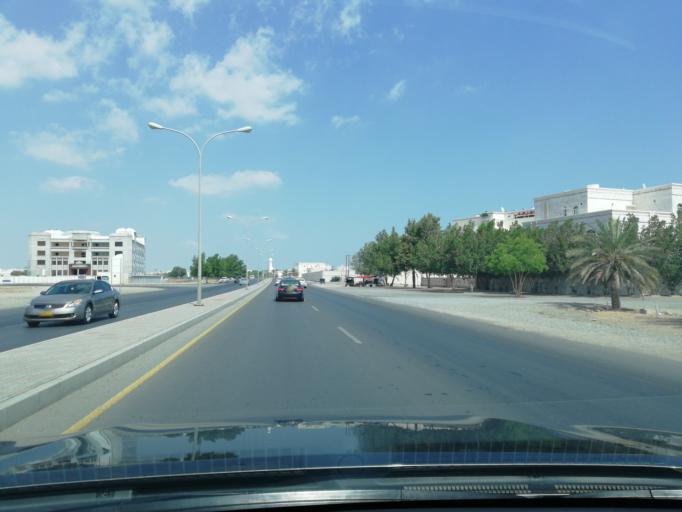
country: OM
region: Muhafazat Masqat
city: As Sib al Jadidah
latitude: 23.6116
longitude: 58.2391
